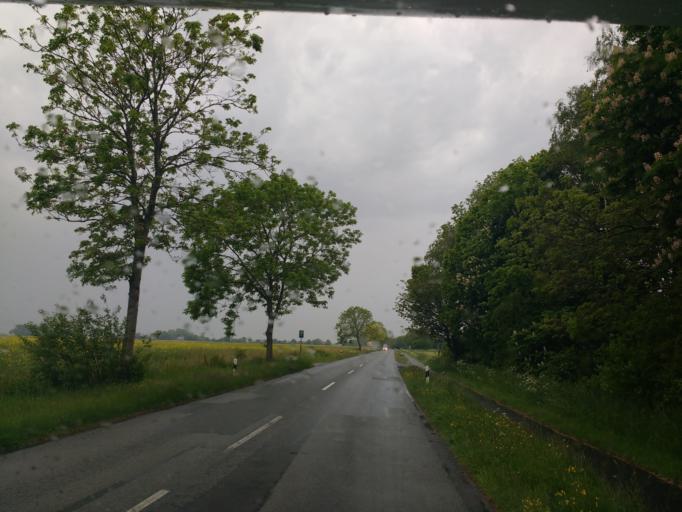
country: DE
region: Lower Saxony
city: Schillig
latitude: 53.6939
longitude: 8.0113
